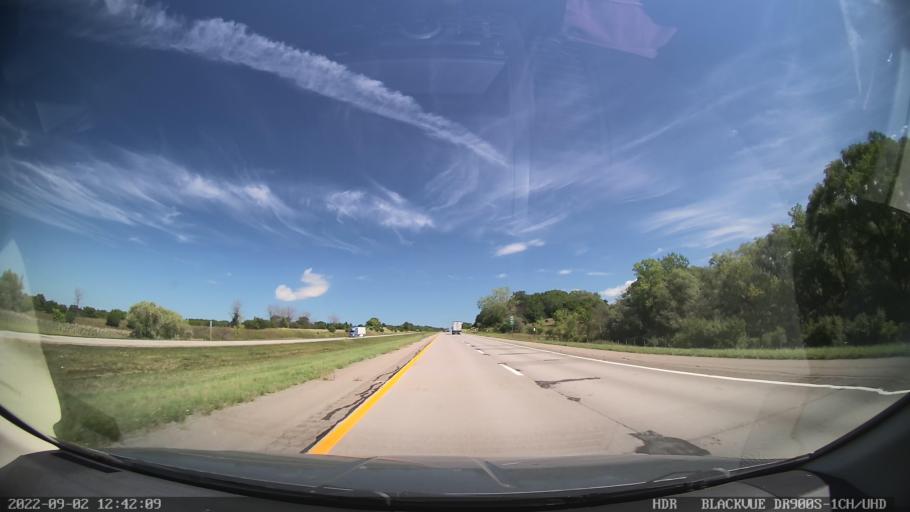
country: US
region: New York
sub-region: Livingston County
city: Geneseo
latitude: 42.7645
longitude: -77.8290
